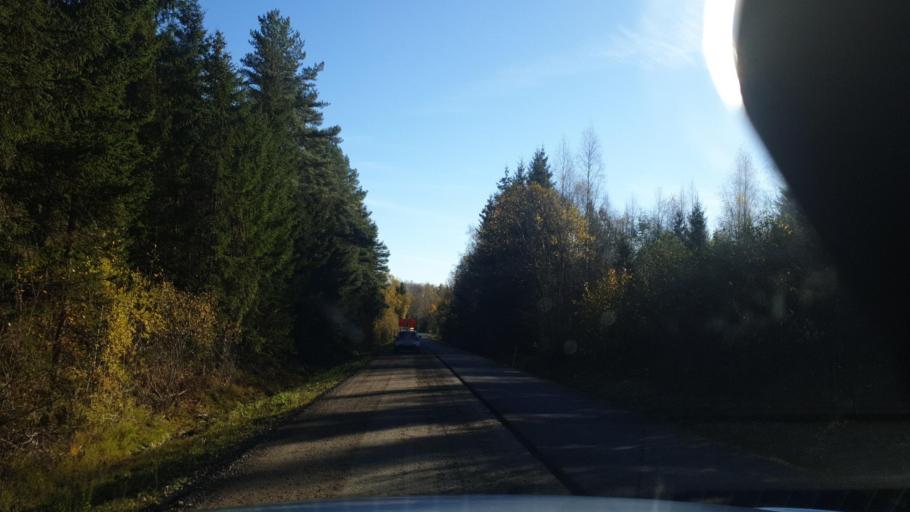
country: SE
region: Vaermland
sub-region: Karlstads Kommun
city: Valberg
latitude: 59.4119
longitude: 13.1726
